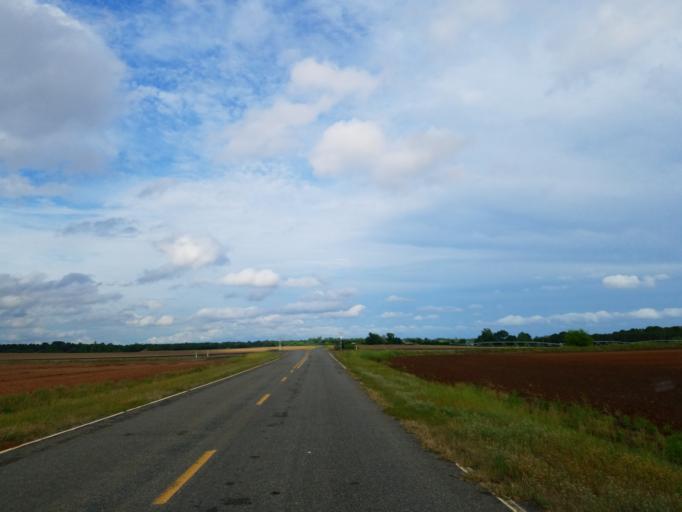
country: US
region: Georgia
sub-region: Dooly County
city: Unadilla
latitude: 32.2129
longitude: -83.7555
